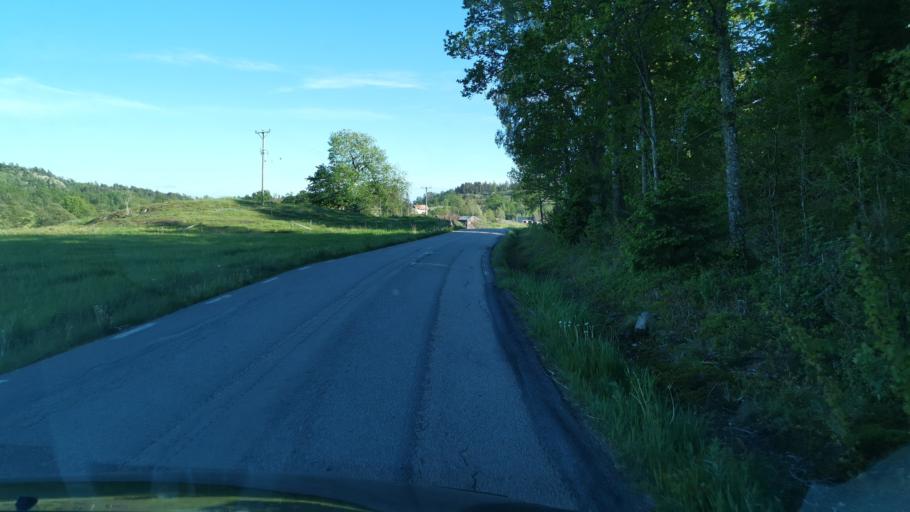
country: SE
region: Vaestra Goetaland
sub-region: Orust
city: Henan
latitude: 58.2785
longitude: 11.5940
